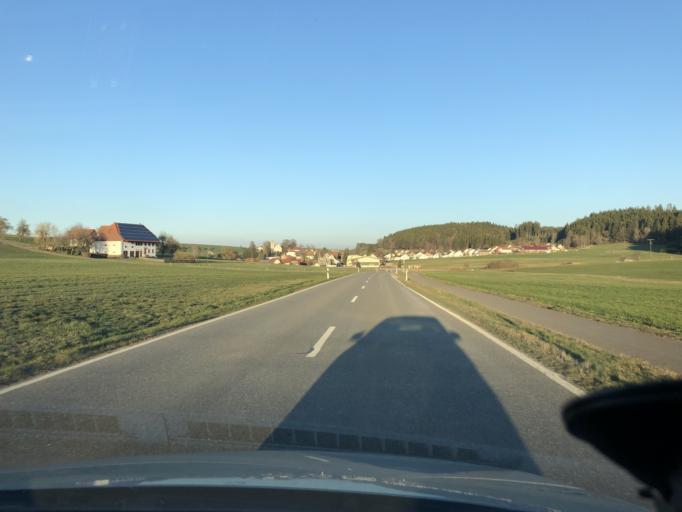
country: DE
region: Baden-Wuerttemberg
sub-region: Freiburg Region
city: Hufingen
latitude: 47.8886
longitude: 8.4798
